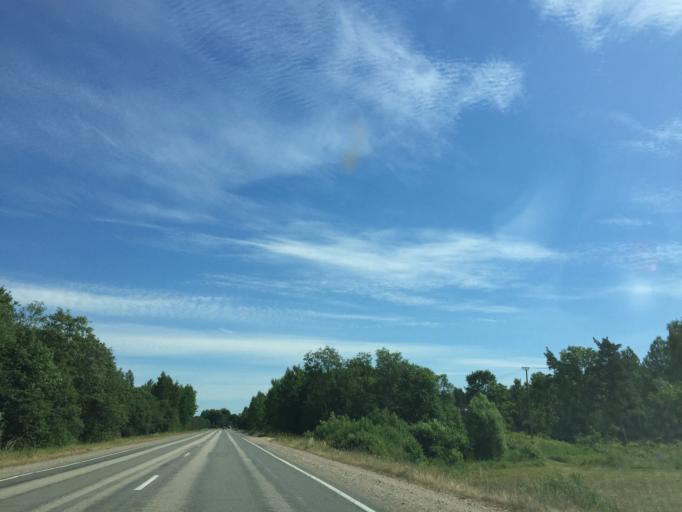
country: LV
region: Skrunda
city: Skrunda
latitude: 56.6739
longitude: 22.0381
